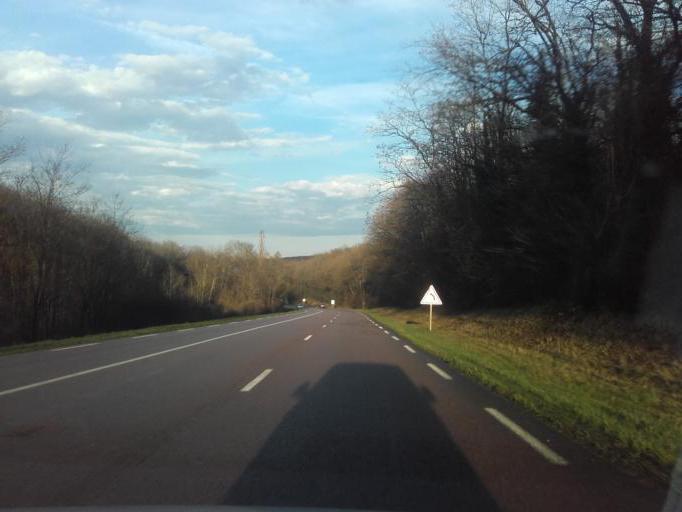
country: FR
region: Bourgogne
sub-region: Departement de la Cote-d'Or
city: Nolay
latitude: 46.9394
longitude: 4.6909
